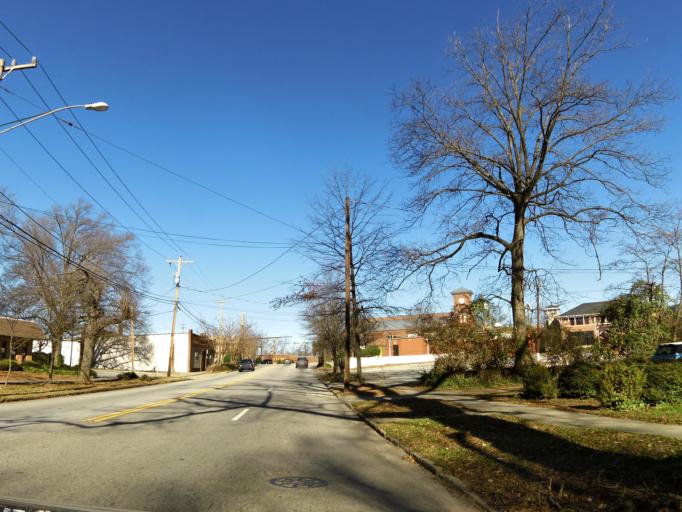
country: US
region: South Carolina
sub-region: Greenville County
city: Greenville
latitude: 34.8557
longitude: -82.4040
